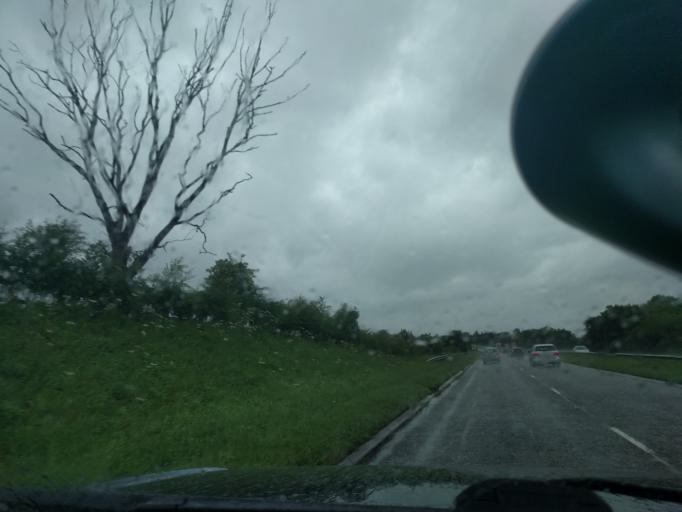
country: GB
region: England
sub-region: Wiltshire
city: Chippenham
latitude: 51.4954
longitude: -2.1265
